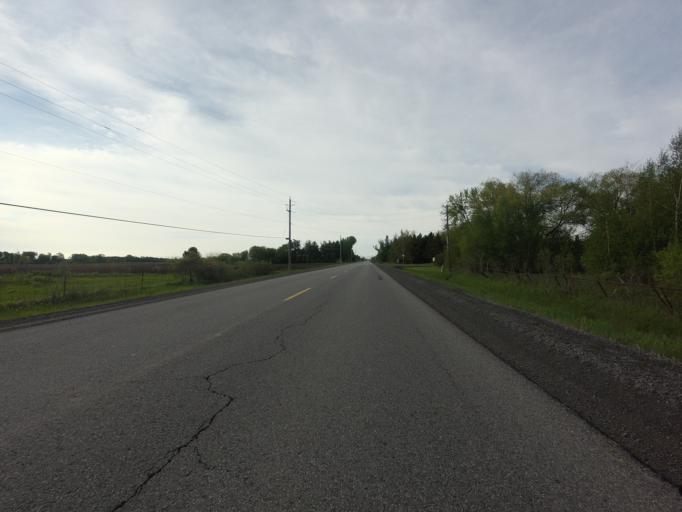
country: CA
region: Ontario
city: Ottawa
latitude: 45.3129
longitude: -75.4606
